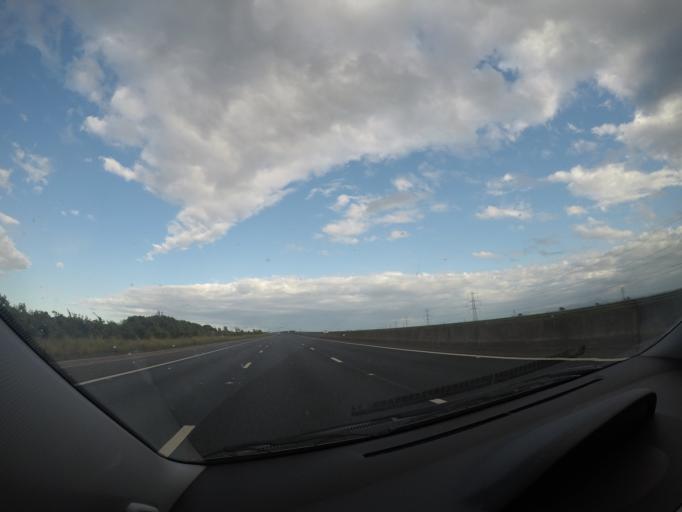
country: GB
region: Scotland
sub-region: Dumfries and Galloway
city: Gretna
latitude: 54.9834
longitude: -3.0305
